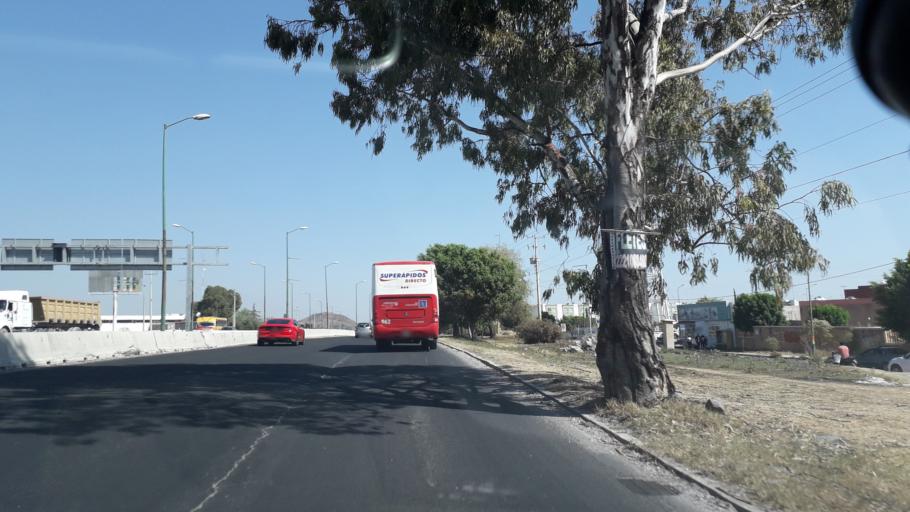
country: MX
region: Puebla
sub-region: Puebla
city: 18 de Marzo
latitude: 18.9772
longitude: -98.2135
